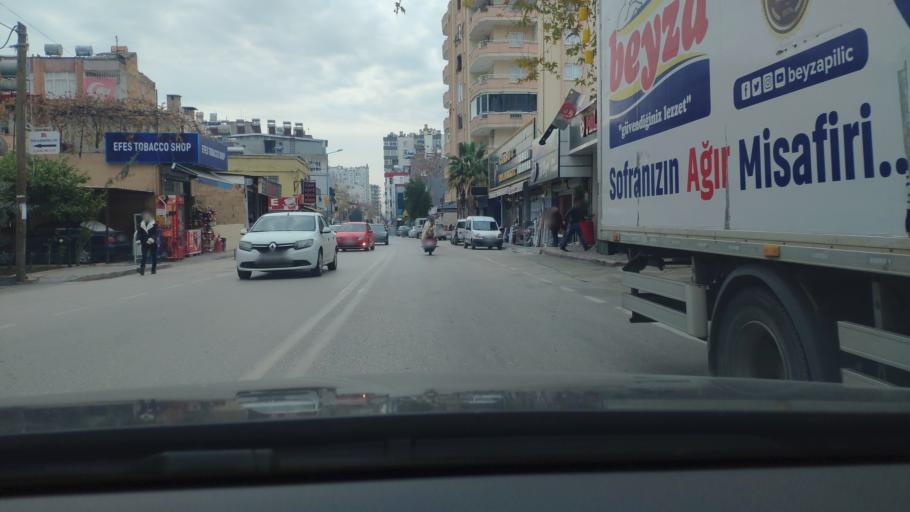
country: TR
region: Adana
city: Adana
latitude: 37.0265
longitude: 35.3118
